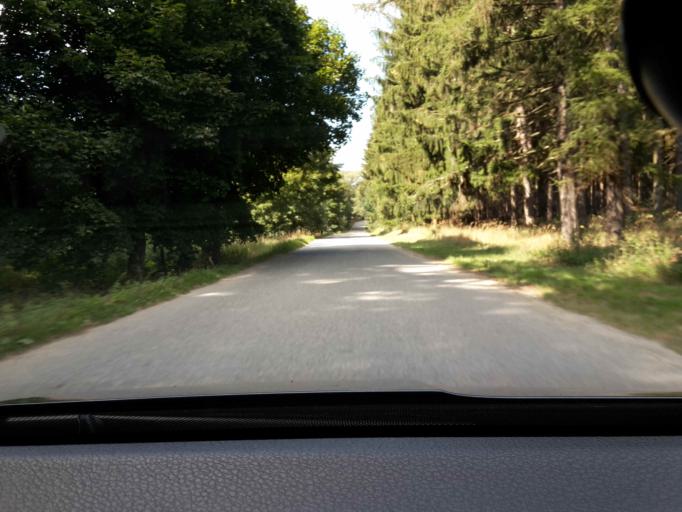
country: CZ
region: Vysocina
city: Zeletava
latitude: 49.1284
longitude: 15.6005
